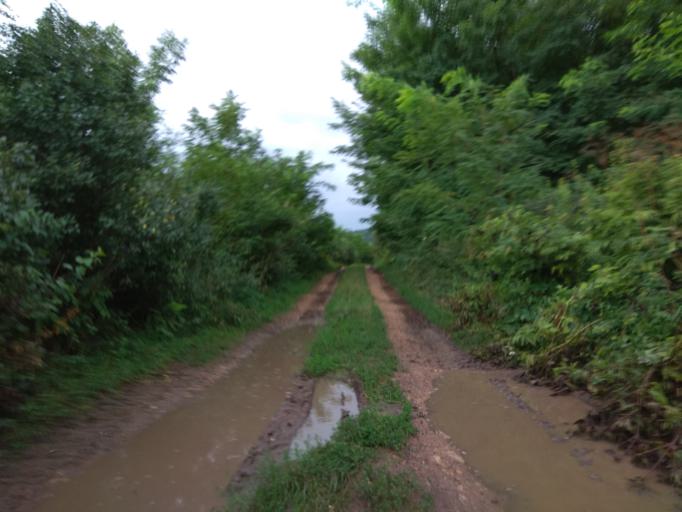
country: HU
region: Borsod-Abauj-Zemplen
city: Monok
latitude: 48.1774
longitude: 21.1228
